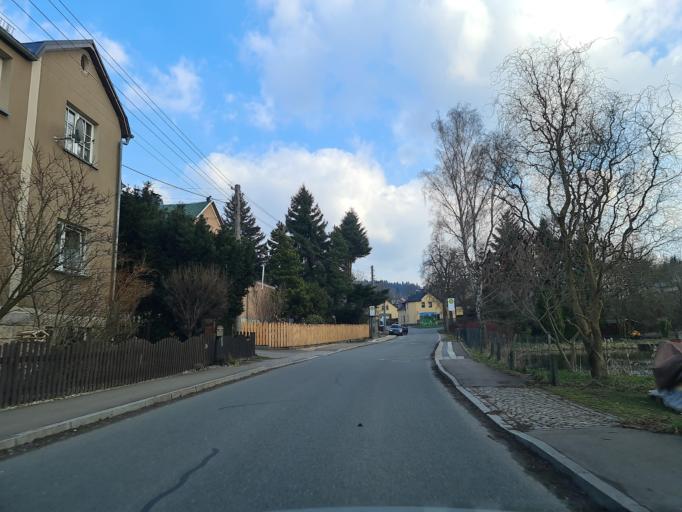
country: DE
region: Saxony
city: Rodewisch
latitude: 50.5210
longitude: 12.4279
